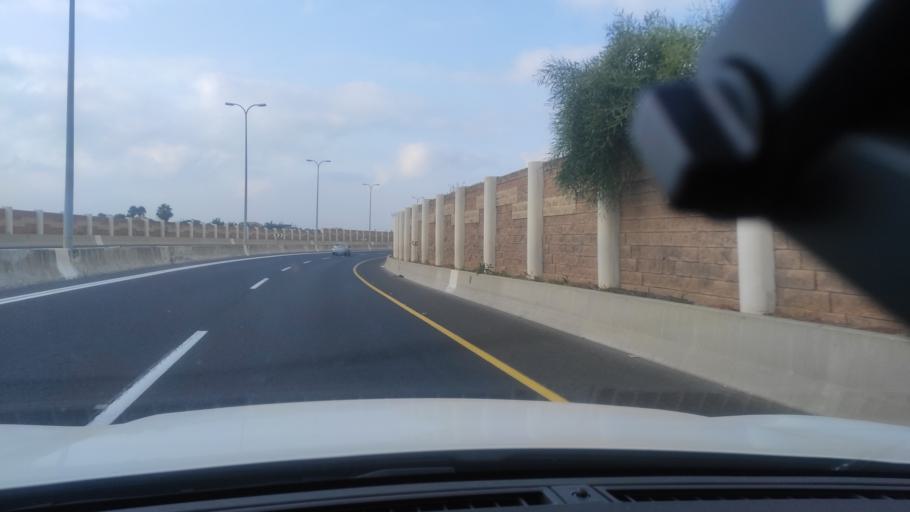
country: IL
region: Central District
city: Kfar Saba
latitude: 32.1592
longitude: 34.9263
